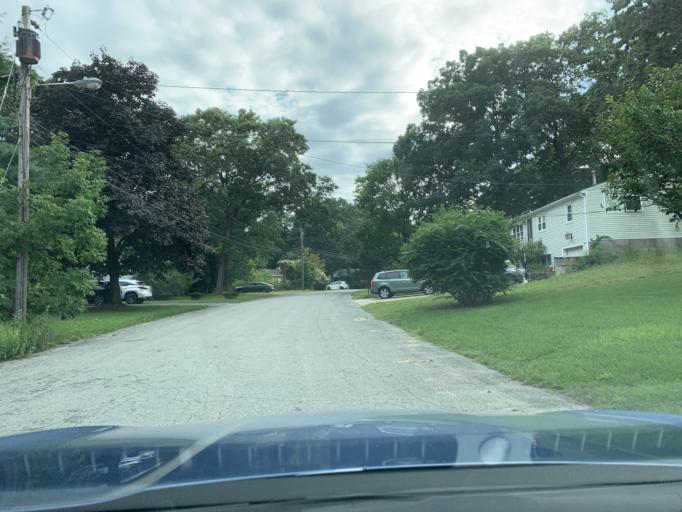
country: US
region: Rhode Island
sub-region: Kent County
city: East Greenwich
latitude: 41.6206
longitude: -71.4524
